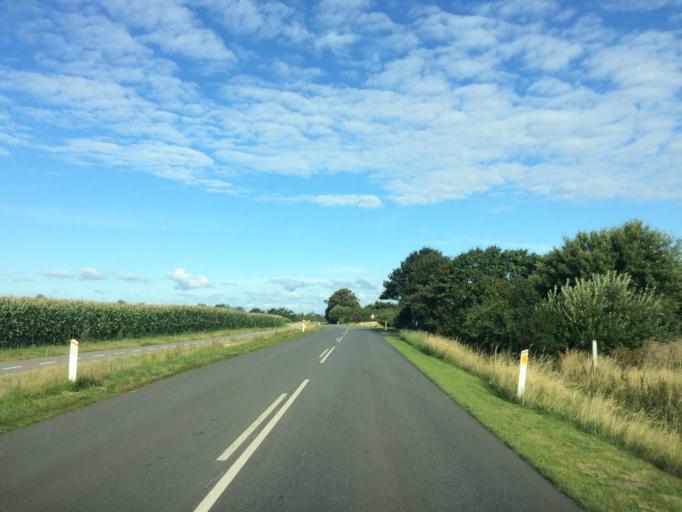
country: DK
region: South Denmark
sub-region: Varde Kommune
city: Oksbol
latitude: 55.8426
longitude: 8.3031
